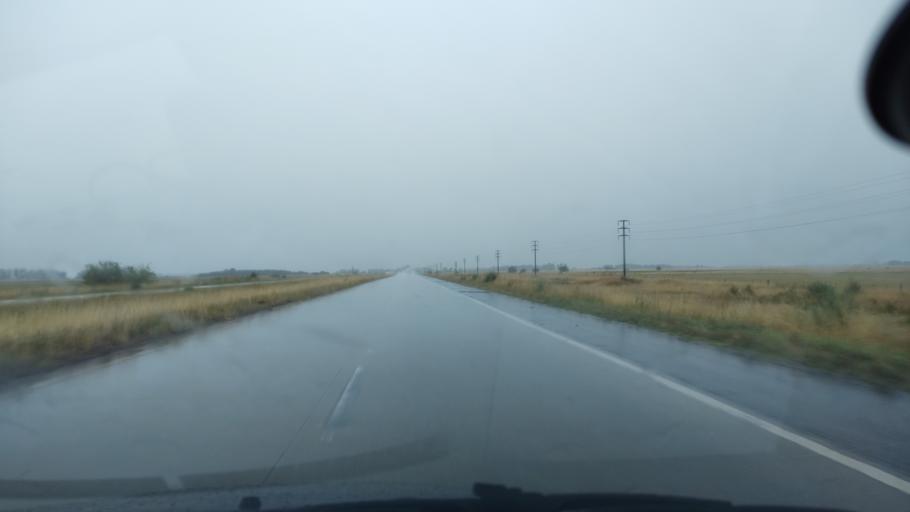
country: AR
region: Buenos Aires
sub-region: Partido de San Vicente
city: San Vicente
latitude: -35.0735
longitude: -58.5400
